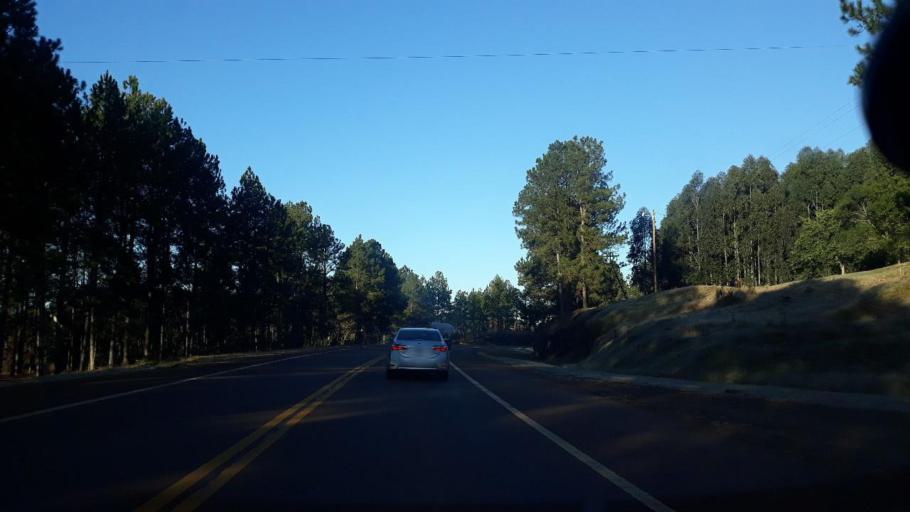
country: AR
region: Misiones
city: San Vicente
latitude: -26.6342
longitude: -54.1261
